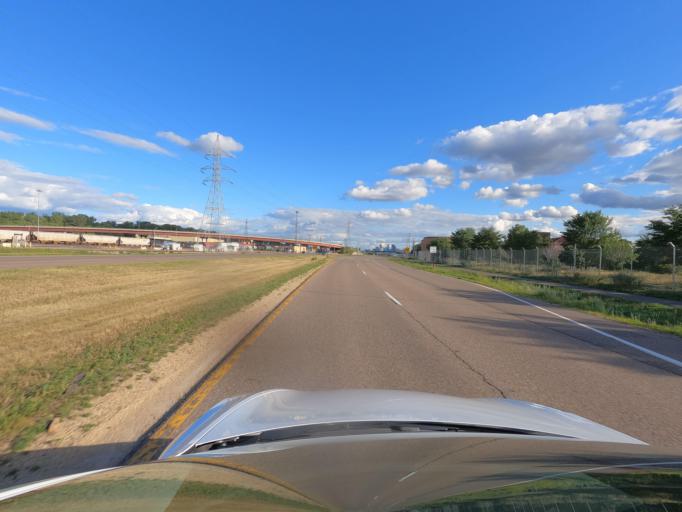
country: US
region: Minnesota
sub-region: Anoka County
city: Columbia Heights
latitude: 45.0479
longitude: -93.2752
